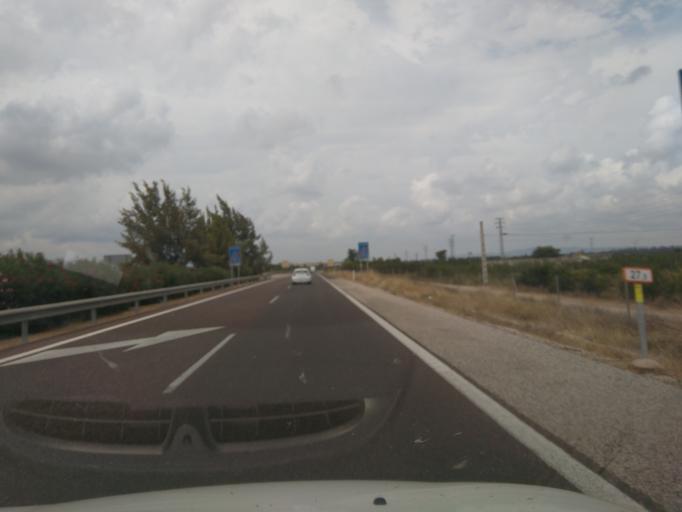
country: ES
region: Valencia
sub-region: Provincia de Valencia
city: L'Alcudia
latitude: 39.1846
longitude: -0.4897
